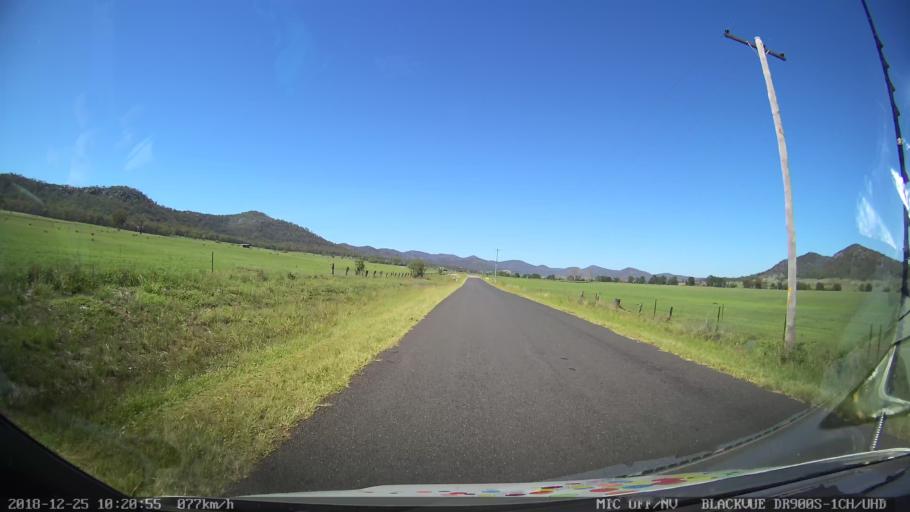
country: AU
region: New South Wales
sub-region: Muswellbrook
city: Denman
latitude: -32.3622
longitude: 150.5447
